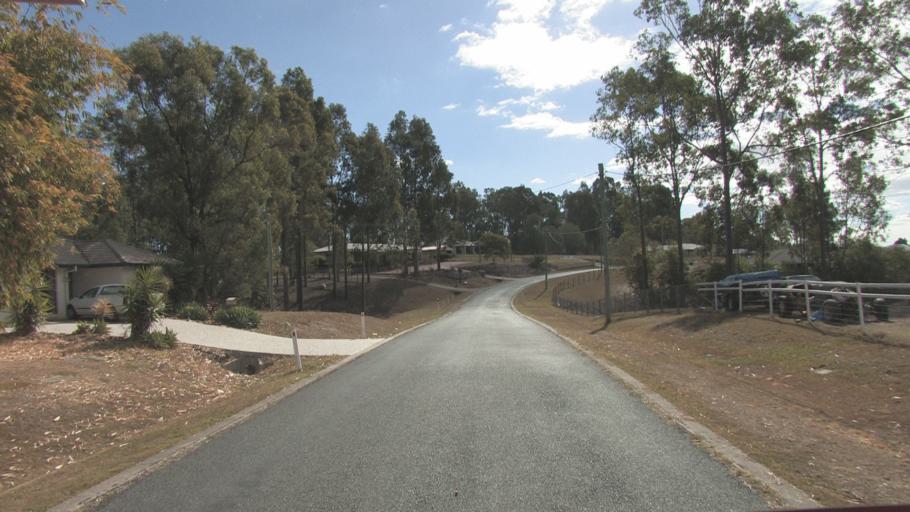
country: AU
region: Queensland
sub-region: Logan
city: Cedar Vale
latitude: -27.8735
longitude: 152.9983
